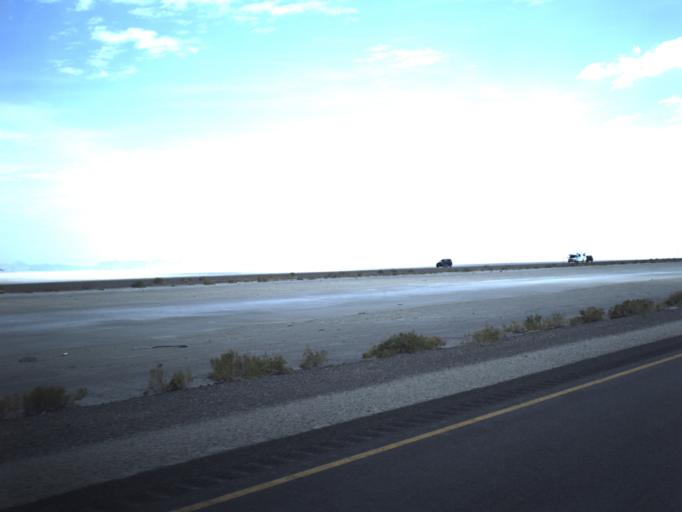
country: US
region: Utah
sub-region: Tooele County
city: Wendover
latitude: 40.7370
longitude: -113.7800
